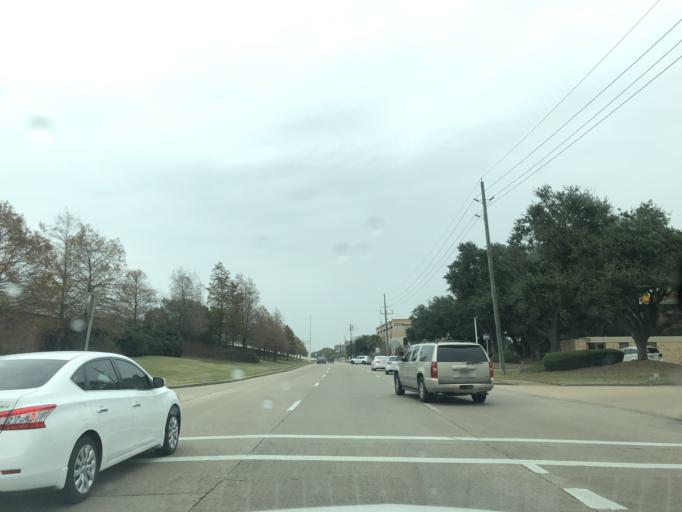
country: US
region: Texas
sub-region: Fort Bend County
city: Sugar Land
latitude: 29.6067
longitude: -95.6133
